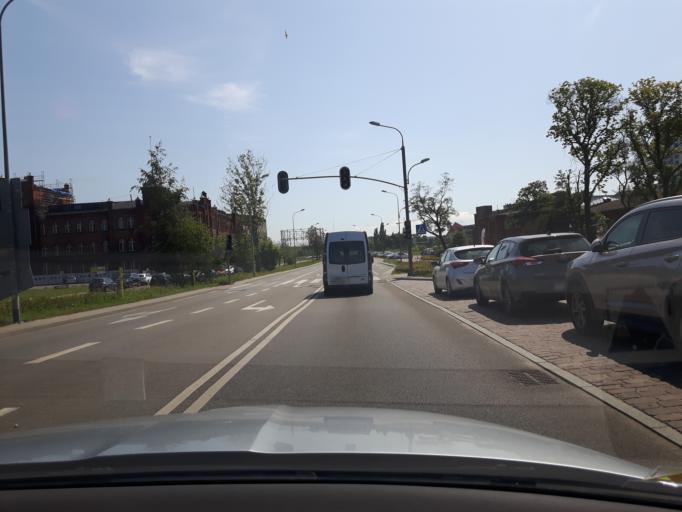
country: PL
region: Pomeranian Voivodeship
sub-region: Gdansk
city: Gdansk
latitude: 54.3623
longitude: 18.6513
